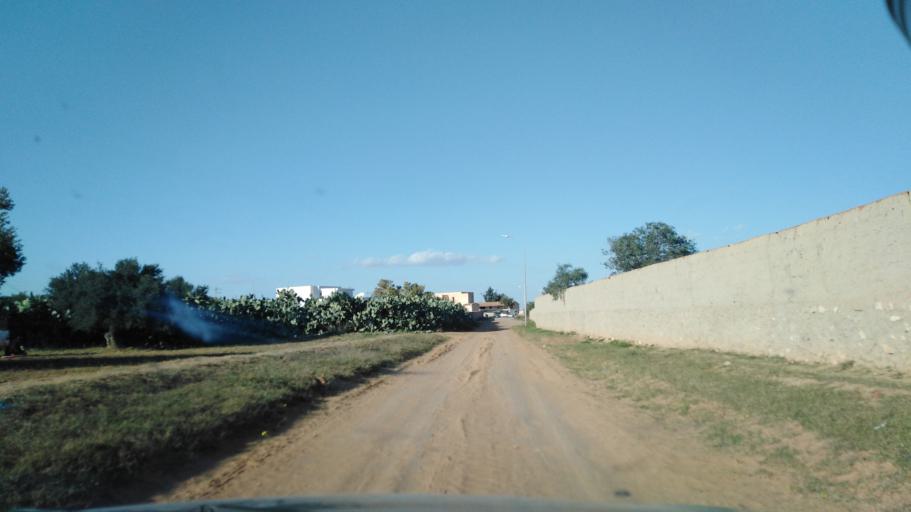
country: TN
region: Al Mahdiyah
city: Shurban
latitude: 34.9581
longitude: 10.3631
